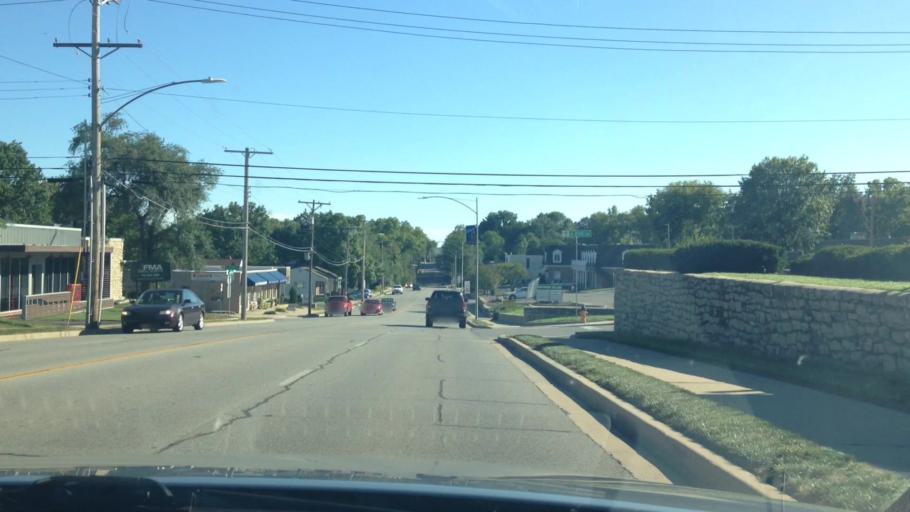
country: US
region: Kansas
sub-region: Johnson County
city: Westwood
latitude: 39.0426
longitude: -94.6120
